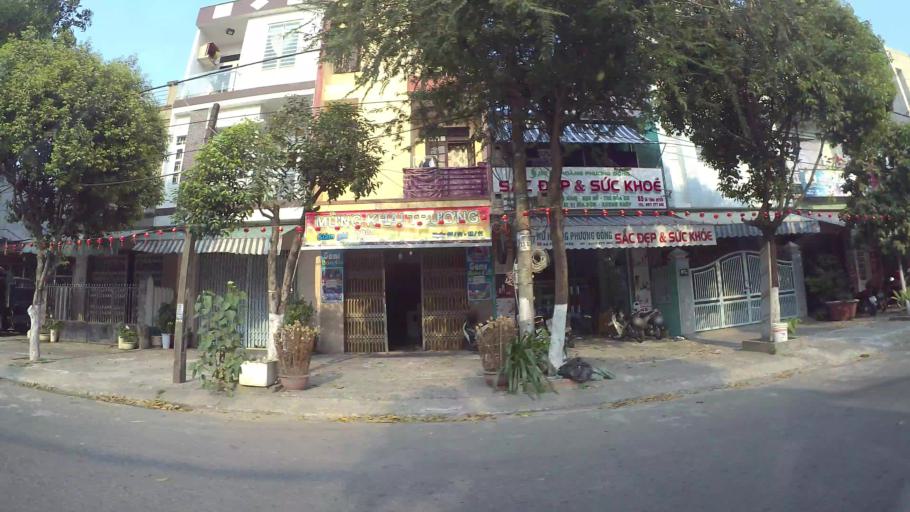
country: VN
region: Da Nang
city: Cam Le
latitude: 16.0193
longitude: 108.2071
